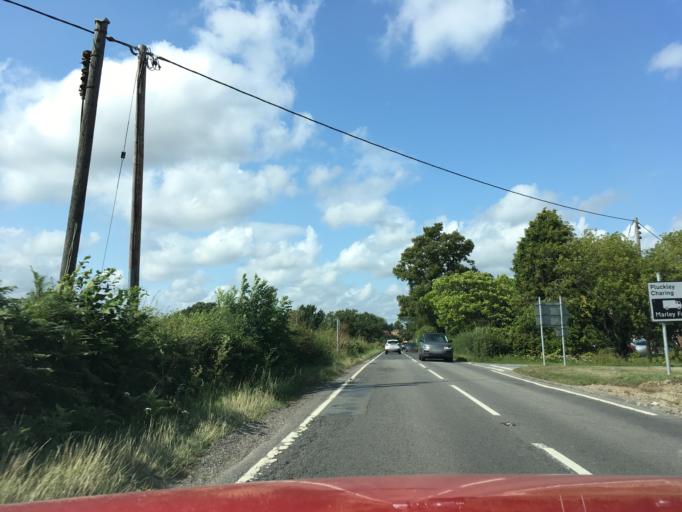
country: GB
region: England
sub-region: Kent
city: Headcorn
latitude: 51.1392
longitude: 0.6412
